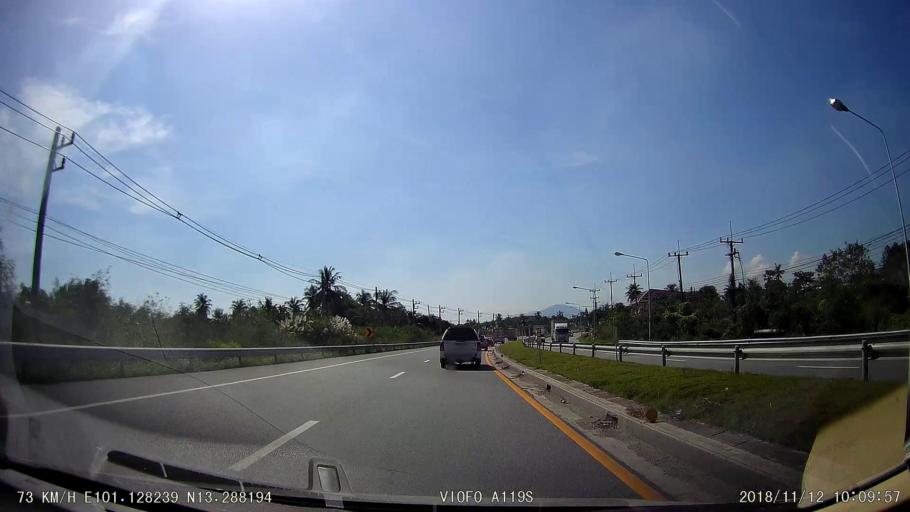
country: TH
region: Chon Buri
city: Ban Bueng
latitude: 13.2879
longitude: 101.1283
